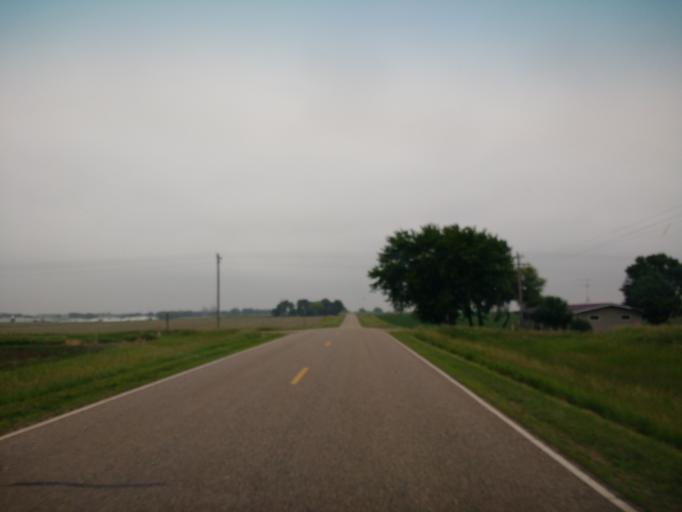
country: US
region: Iowa
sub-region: Sioux County
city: Alton
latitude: 43.0543
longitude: -95.8995
